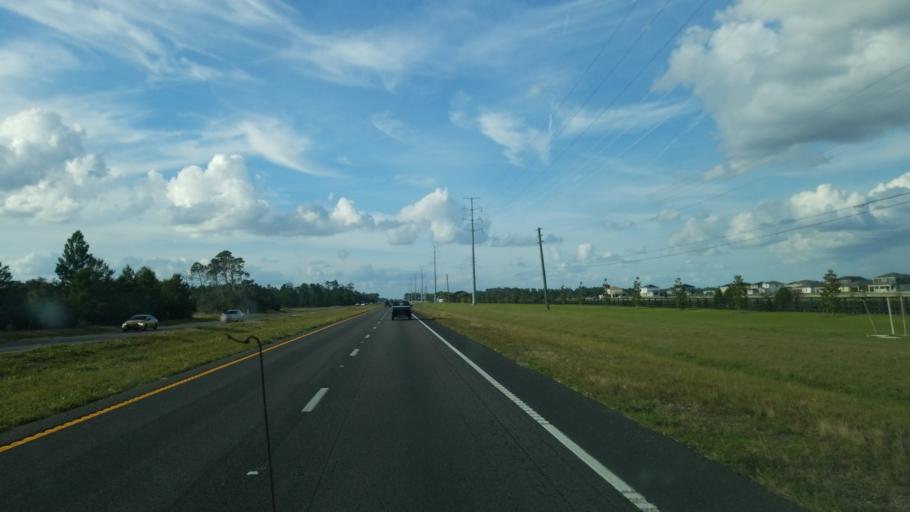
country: US
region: Florida
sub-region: Osceola County
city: Saint Cloud
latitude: 28.2068
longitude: -81.1707
